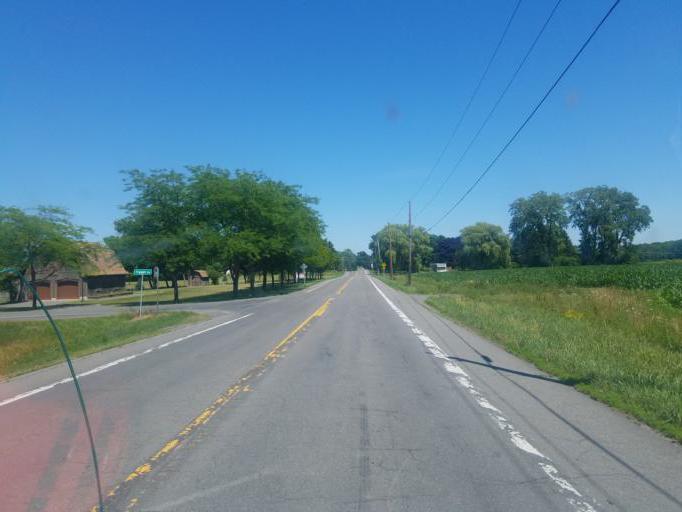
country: US
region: New York
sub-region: Ontario County
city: Geneva
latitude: 42.8413
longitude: -77.0362
